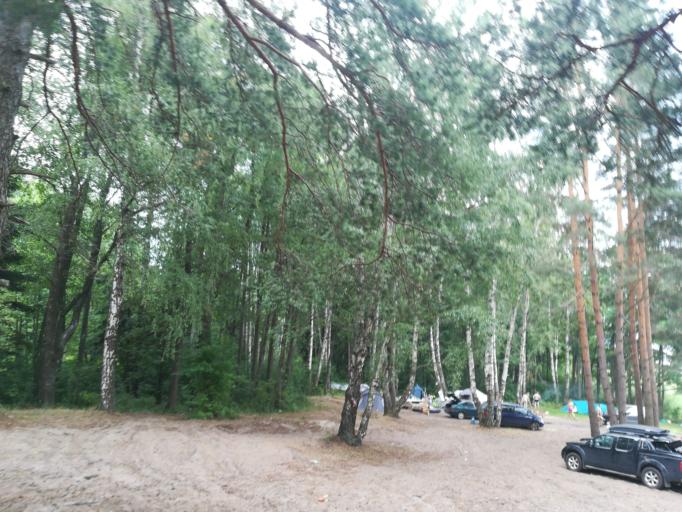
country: RU
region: Leningrad
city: Ust'-Luga
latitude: 59.7512
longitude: 28.1546
